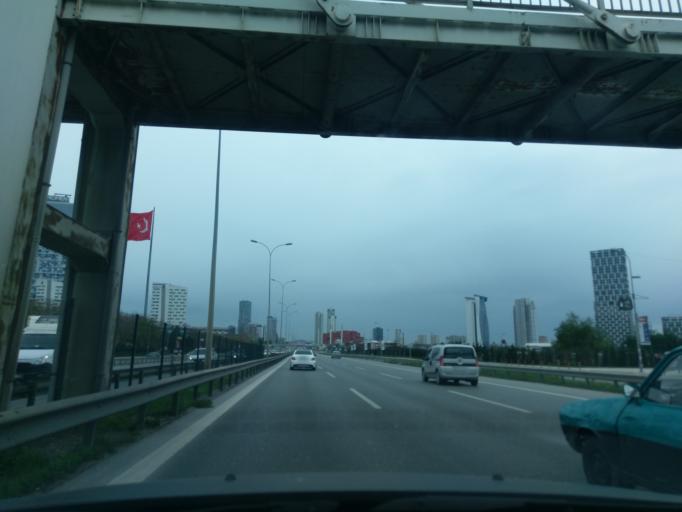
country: TR
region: Istanbul
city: Maltepe
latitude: 40.9158
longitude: 29.1818
